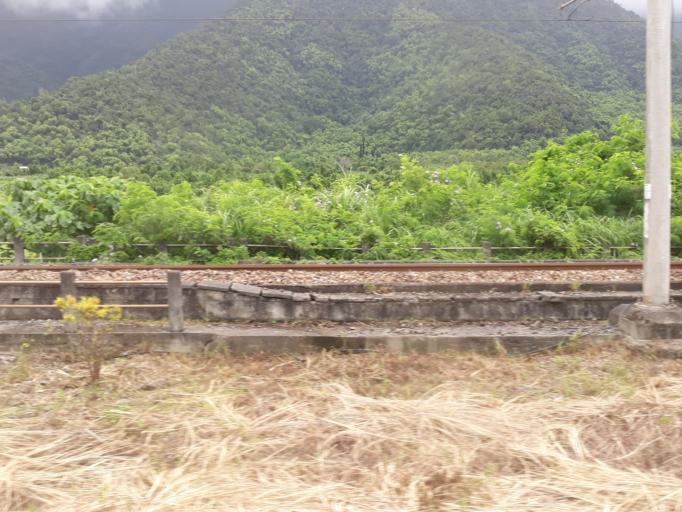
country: TW
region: Taiwan
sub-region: Yilan
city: Yilan
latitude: 24.4620
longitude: 121.8098
